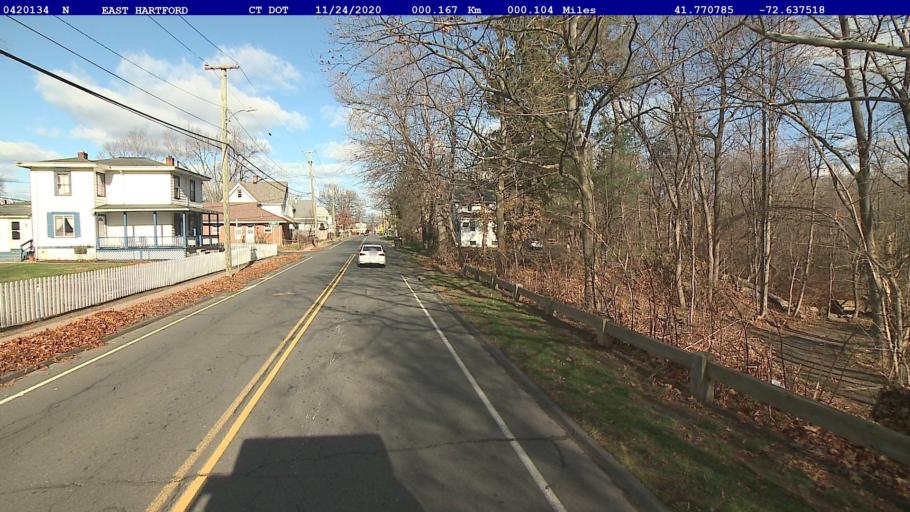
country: US
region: Connecticut
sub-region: Hartford County
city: East Hartford
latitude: 41.7708
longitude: -72.6375
